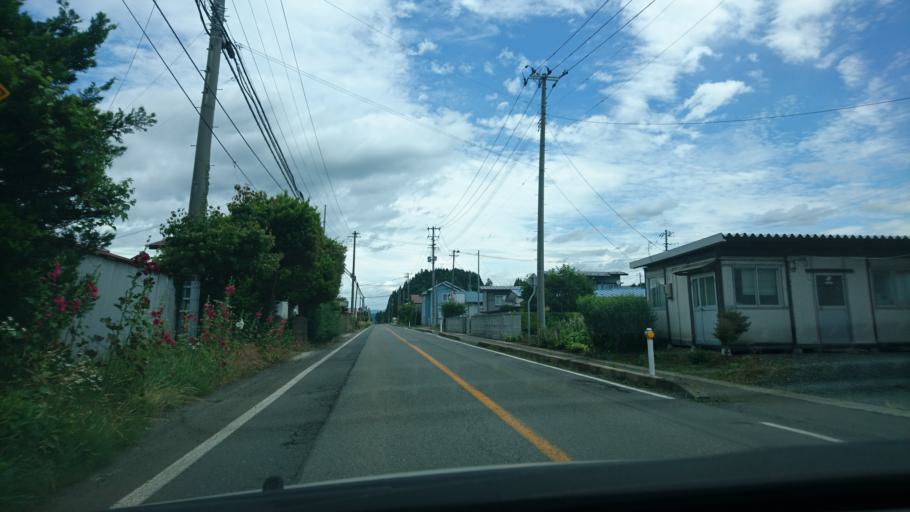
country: JP
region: Iwate
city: Morioka-shi
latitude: 39.5606
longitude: 141.1780
